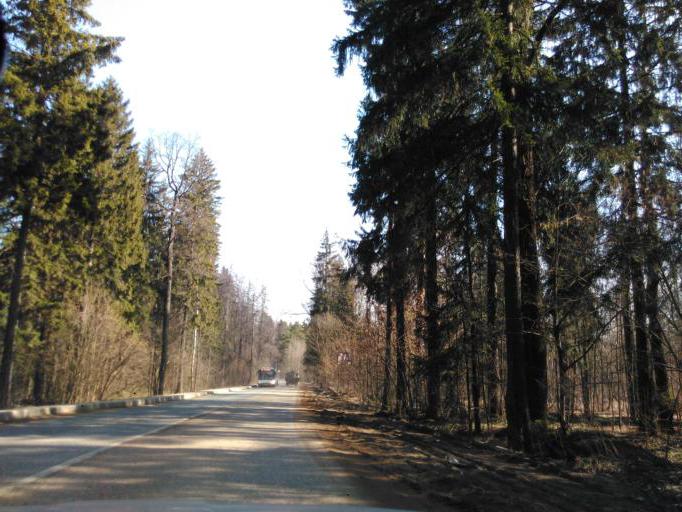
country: RU
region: Moskovskaya
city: Opalikha
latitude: 55.8890
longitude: 37.2663
